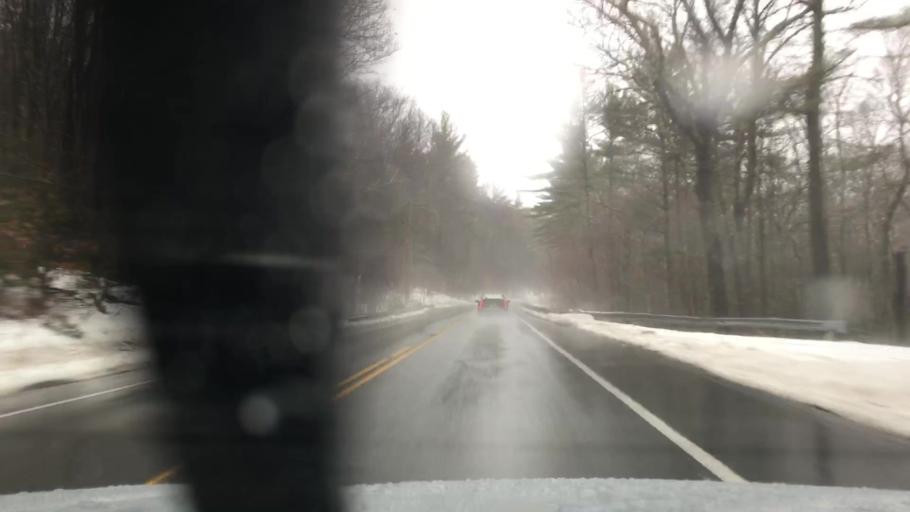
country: US
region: Massachusetts
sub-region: Franklin County
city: Wendell
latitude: 42.5100
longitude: -72.3285
